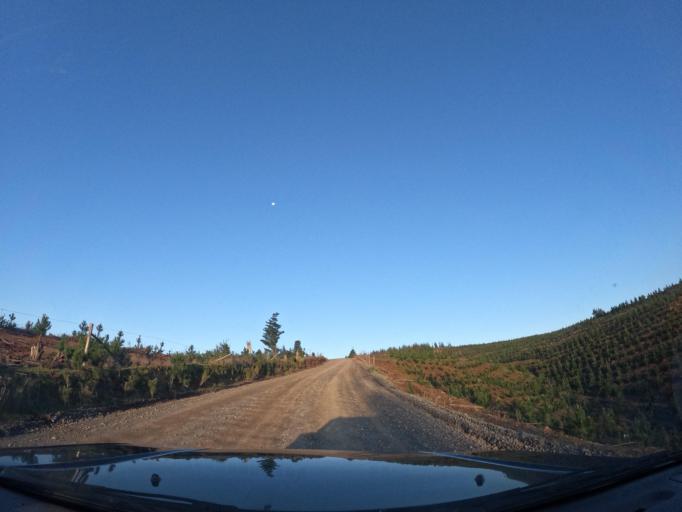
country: CL
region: Biobio
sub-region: Provincia de Concepcion
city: Chiguayante
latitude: -37.0099
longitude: -72.8898
